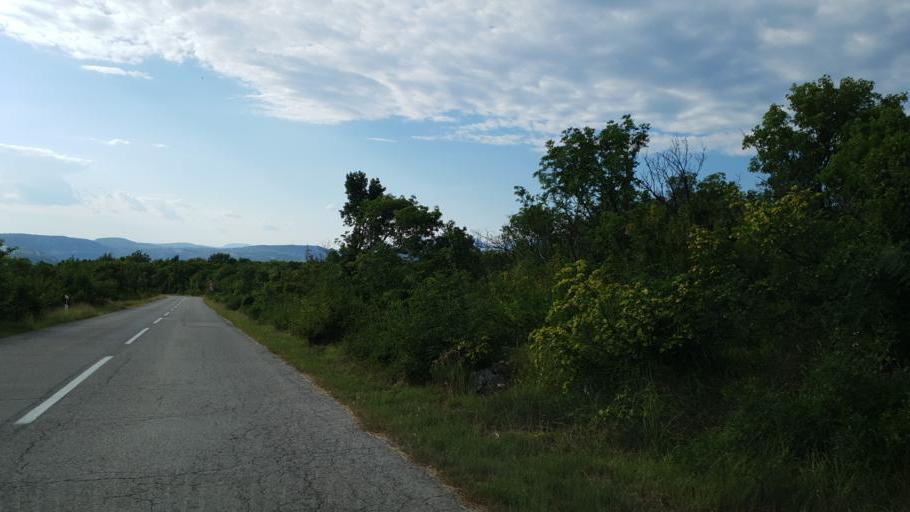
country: HR
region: Primorsko-Goranska
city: Hreljin
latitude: 45.2698
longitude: 14.5871
